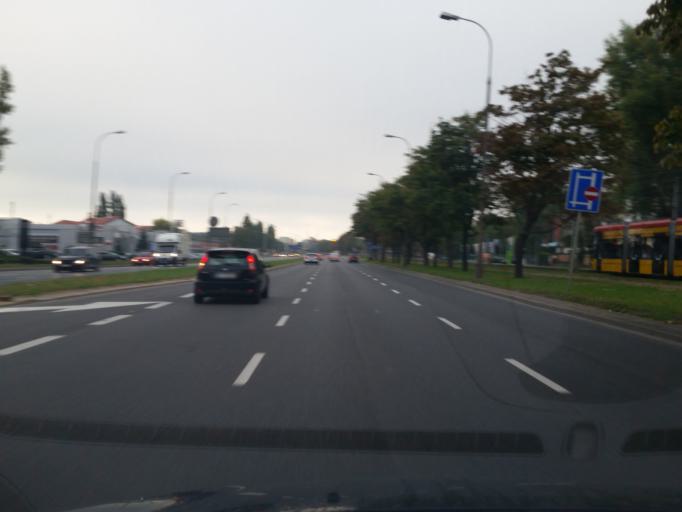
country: PL
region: Masovian Voivodeship
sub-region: Warszawa
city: Zoliborz
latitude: 52.2767
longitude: 21.0131
